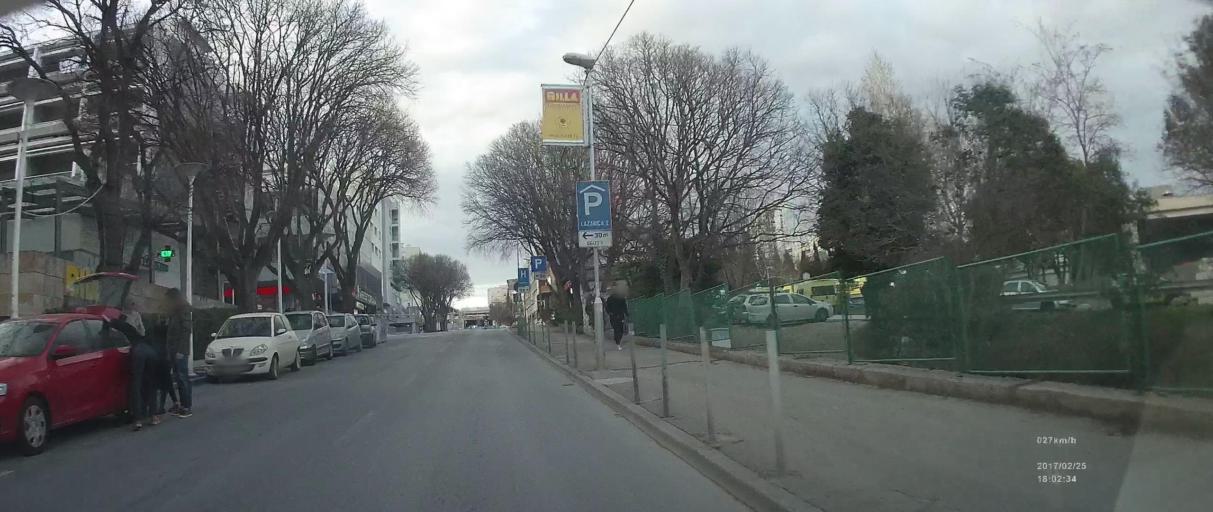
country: HR
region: Splitsko-Dalmatinska
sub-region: Grad Split
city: Split
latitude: 43.5037
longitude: 16.4567
